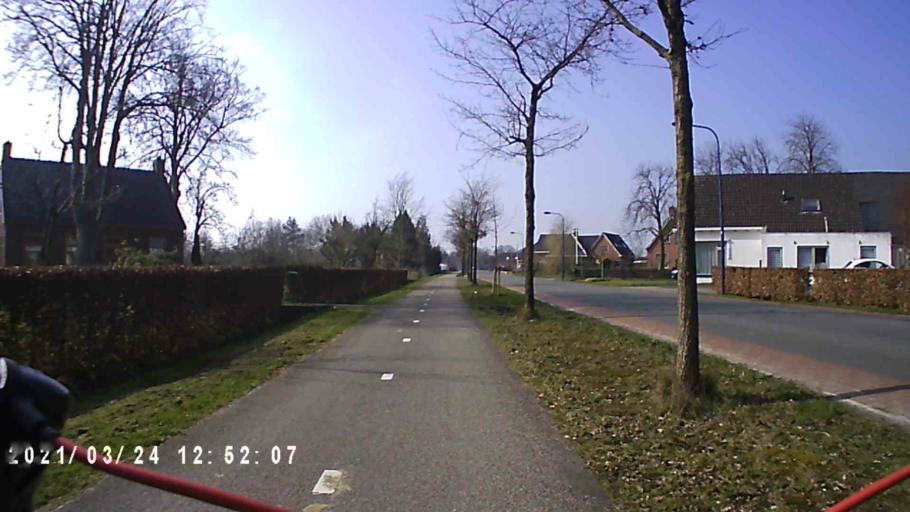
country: NL
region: Groningen
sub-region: Gemeente Leek
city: Leek
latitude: 53.1598
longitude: 6.3243
